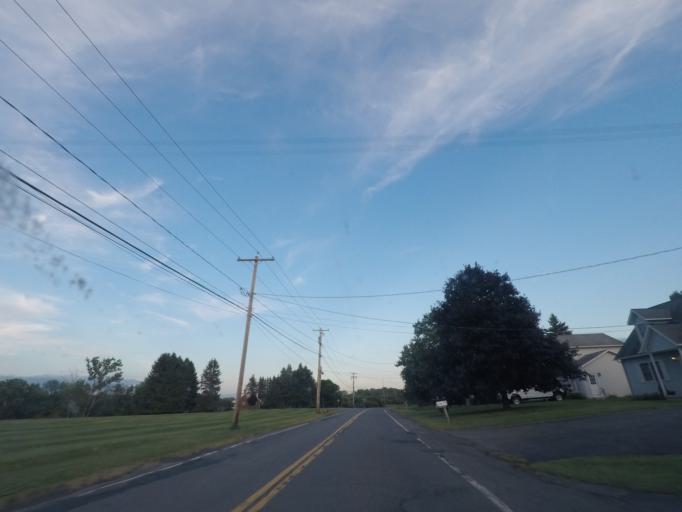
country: US
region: New York
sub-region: Albany County
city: Cohoes
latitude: 42.7645
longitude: -73.7708
